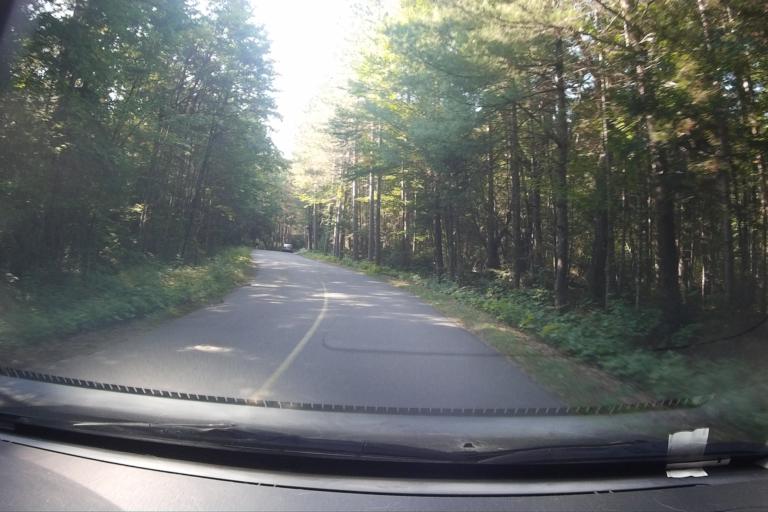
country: CA
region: Ontario
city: Huntsville
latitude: 45.5567
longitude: -78.5999
